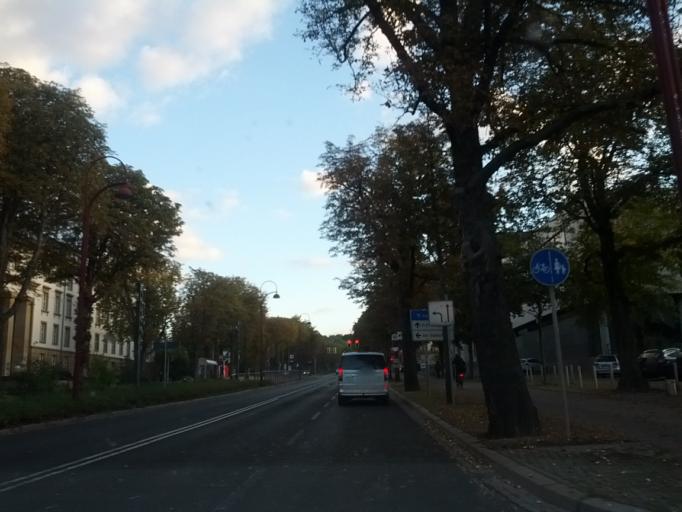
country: DE
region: Thuringia
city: Erfurt
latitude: 50.9644
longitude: 11.0332
